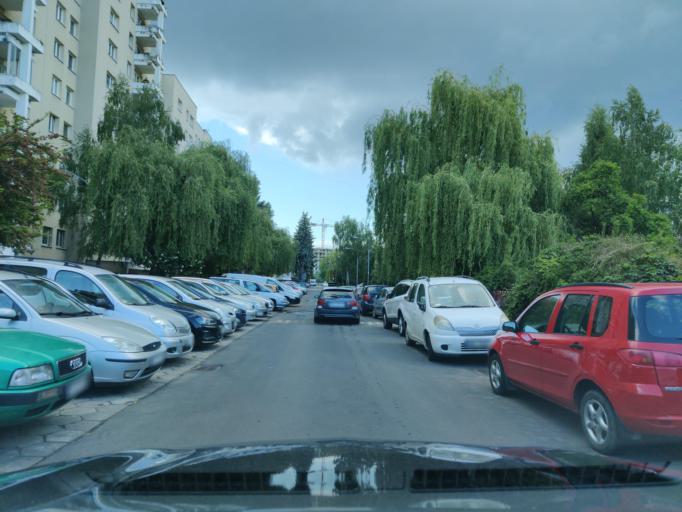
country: PL
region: Masovian Voivodeship
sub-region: Warszawa
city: Mokotow
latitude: 52.1748
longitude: 21.0278
